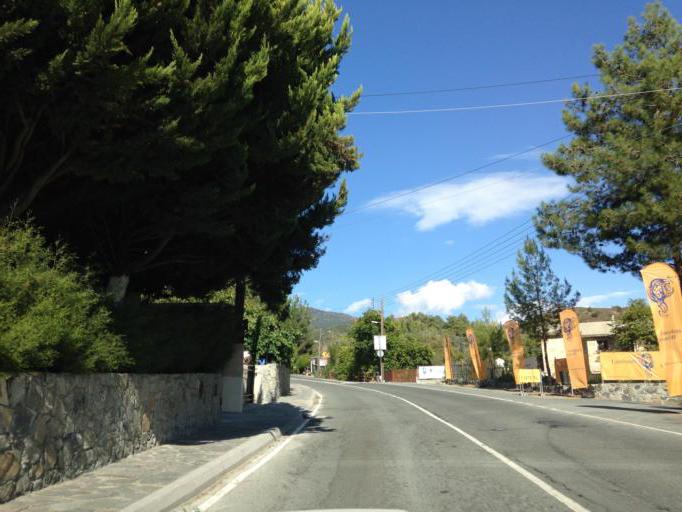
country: CY
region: Limassol
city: Pachna
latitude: 34.8762
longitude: 32.8367
